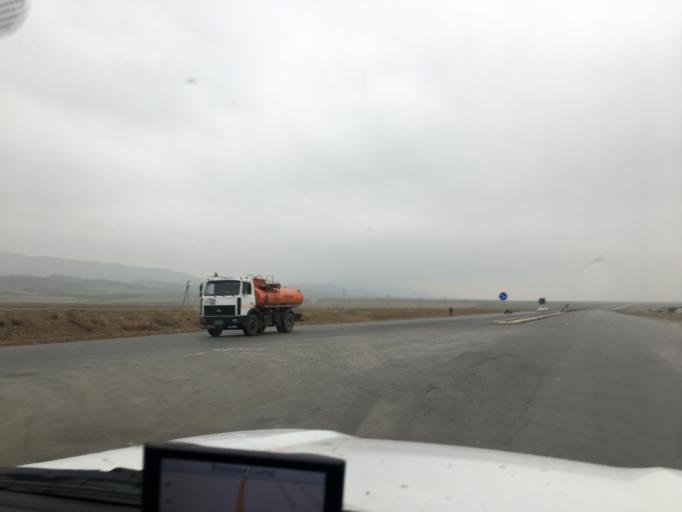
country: IR
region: Razavi Khorasan
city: Dargaz
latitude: 37.7689
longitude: 58.8931
